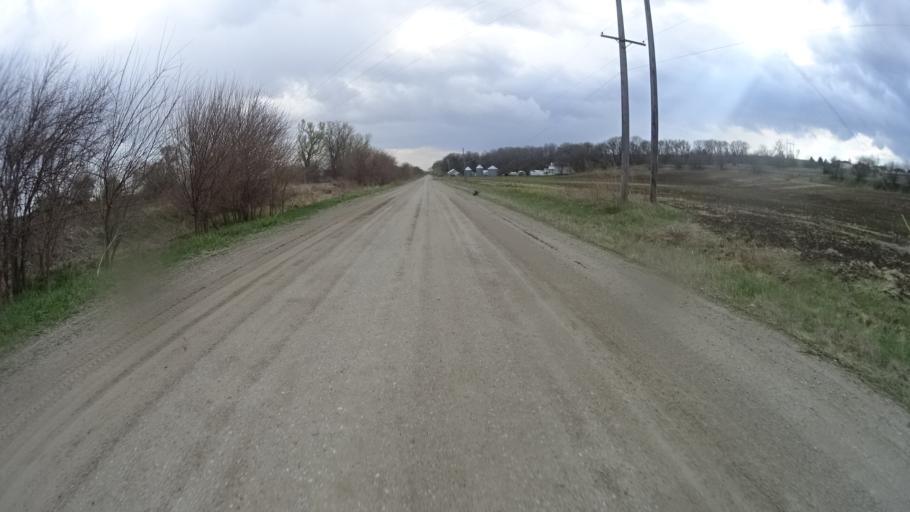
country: US
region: Nebraska
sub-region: Sarpy County
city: Offutt Air Force Base
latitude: 41.0906
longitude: -95.9147
